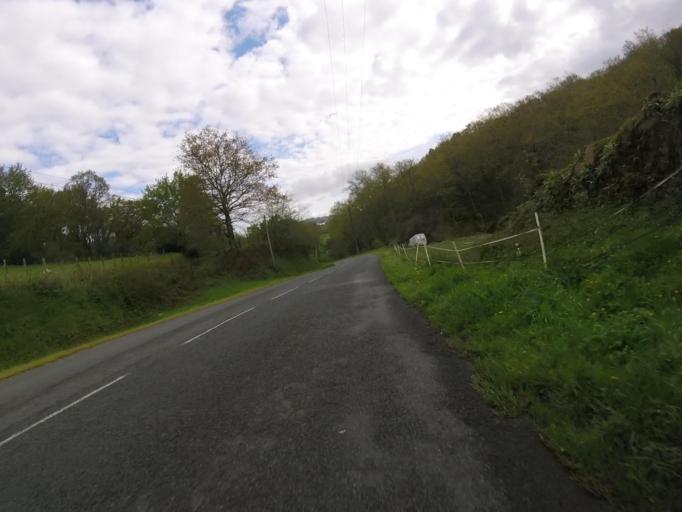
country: FR
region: Aquitaine
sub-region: Departement des Pyrenees-Atlantiques
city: Sare
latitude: 43.2934
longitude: -1.5932
